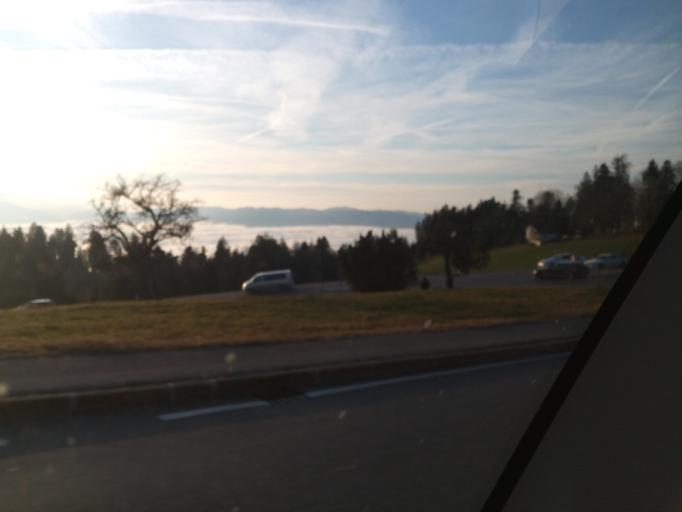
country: AT
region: Vorarlberg
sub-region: Politischer Bezirk Bregenz
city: Bildstein
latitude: 47.4301
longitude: 9.7843
